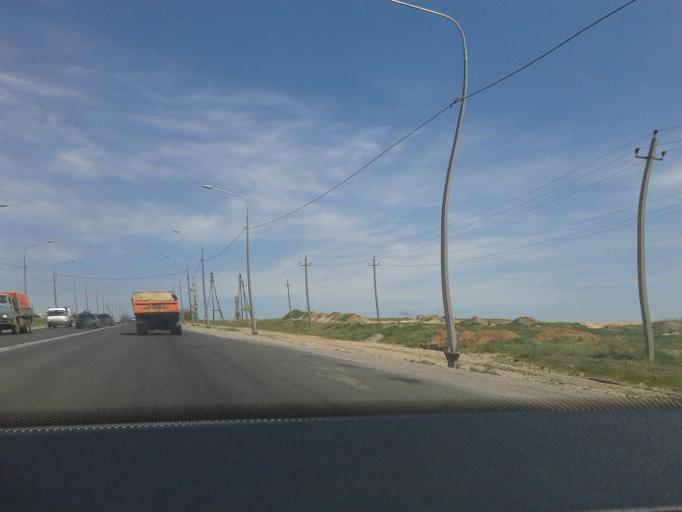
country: RU
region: Volgograd
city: Vodstroy
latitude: 48.8097
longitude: 44.5236
